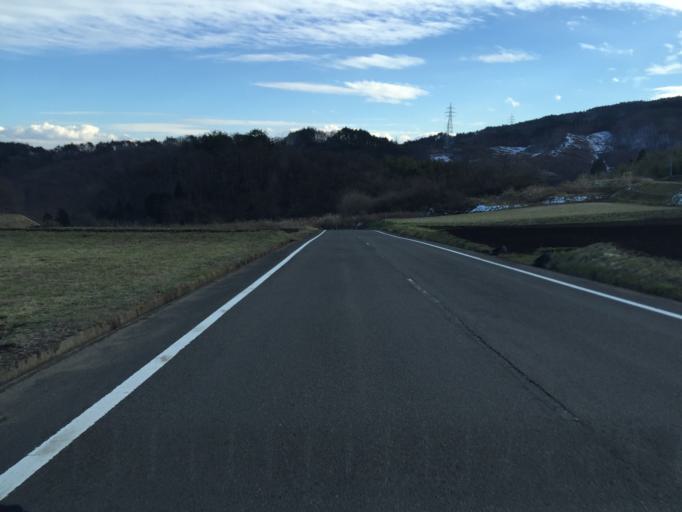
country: JP
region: Fukushima
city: Fukushima-shi
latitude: 37.7005
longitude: 140.3856
